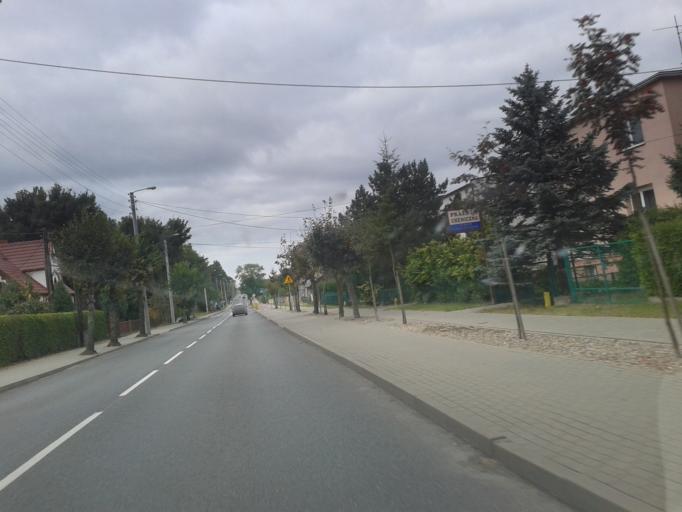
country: PL
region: Kujawsko-Pomorskie
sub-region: Powiat sepolenski
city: Sepolno Krajenskie
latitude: 53.4573
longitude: 17.5334
